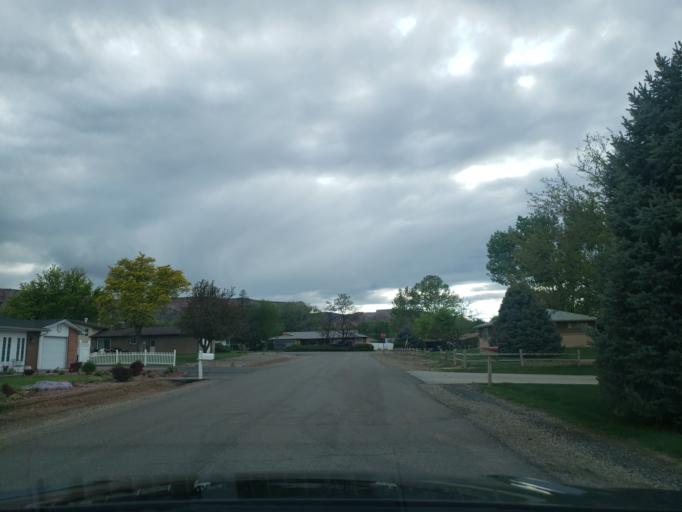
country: US
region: Colorado
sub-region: Mesa County
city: Redlands
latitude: 39.0973
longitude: -108.6611
